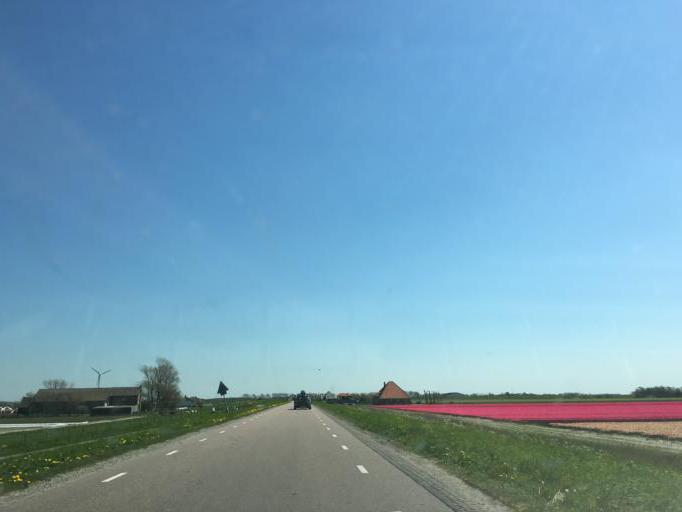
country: NL
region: North Holland
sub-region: Gemeente Schagen
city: Schagen
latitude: 52.8534
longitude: 4.7343
